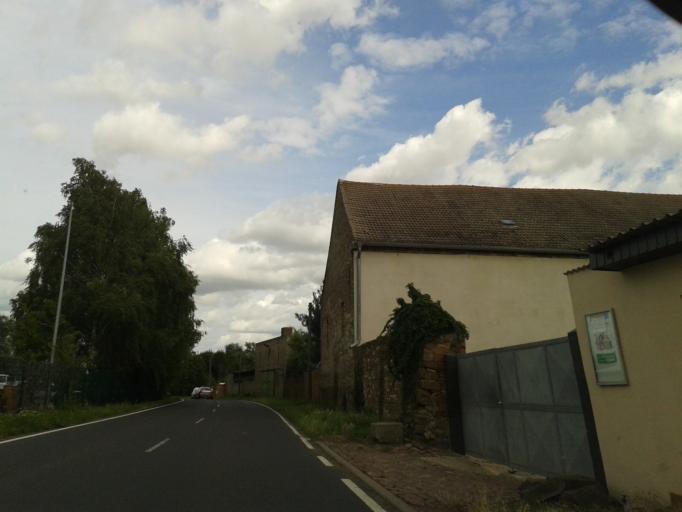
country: DE
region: Saxony-Anhalt
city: Peissen
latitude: 51.5099
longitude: 12.0335
